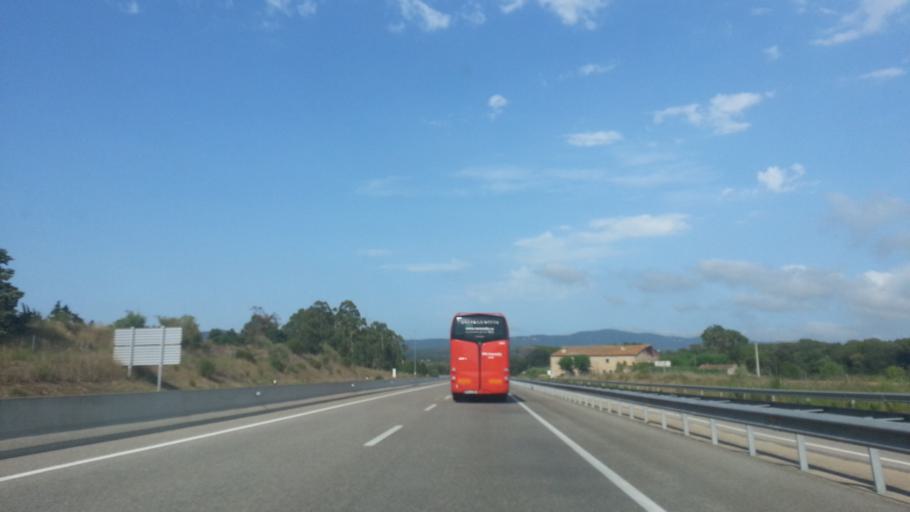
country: ES
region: Catalonia
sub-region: Provincia de Girona
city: Llagostera
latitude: 41.8237
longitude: 2.9136
